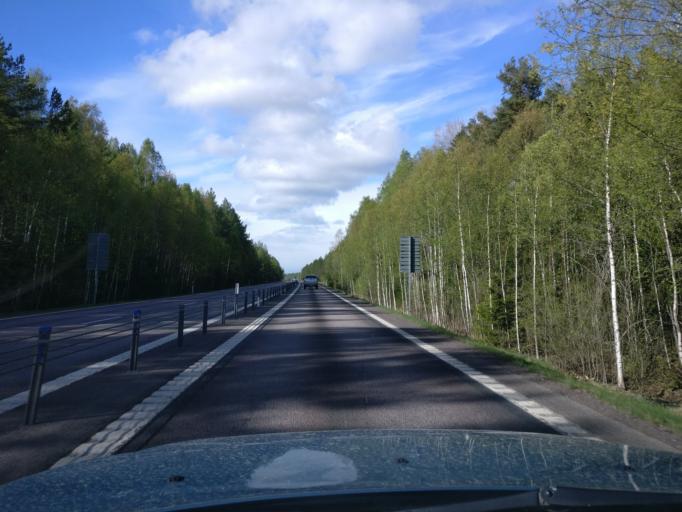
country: SE
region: Vaermland
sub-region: Forshaga Kommun
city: Forshaga
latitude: 59.4488
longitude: 13.4169
